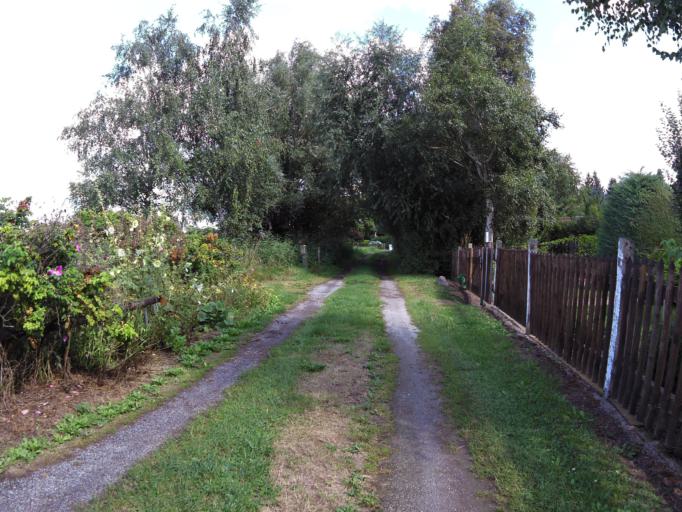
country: DE
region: Brandenburg
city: Storkow
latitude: 52.2593
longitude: 13.9285
